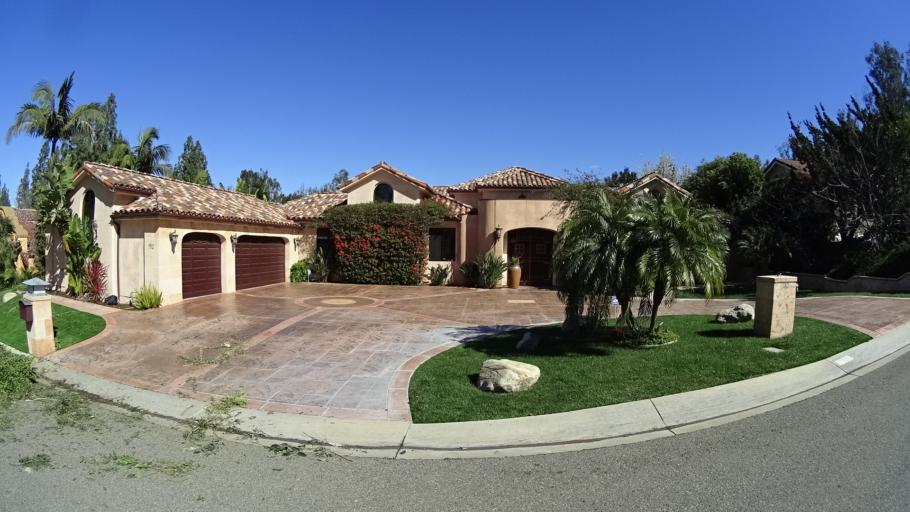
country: US
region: California
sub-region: Orange County
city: Villa Park
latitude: 33.8453
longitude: -117.8105
